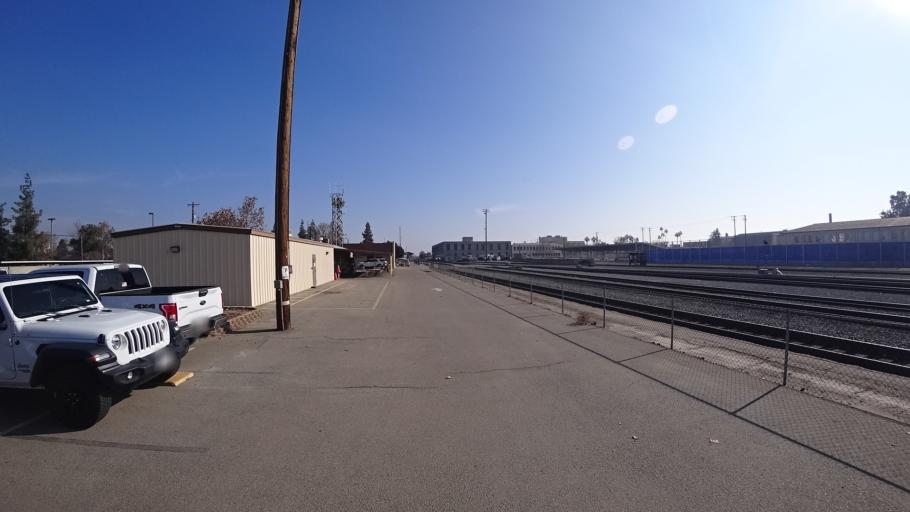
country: US
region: California
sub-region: Kern County
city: Bakersfield
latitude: 35.3715
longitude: -119.0259
